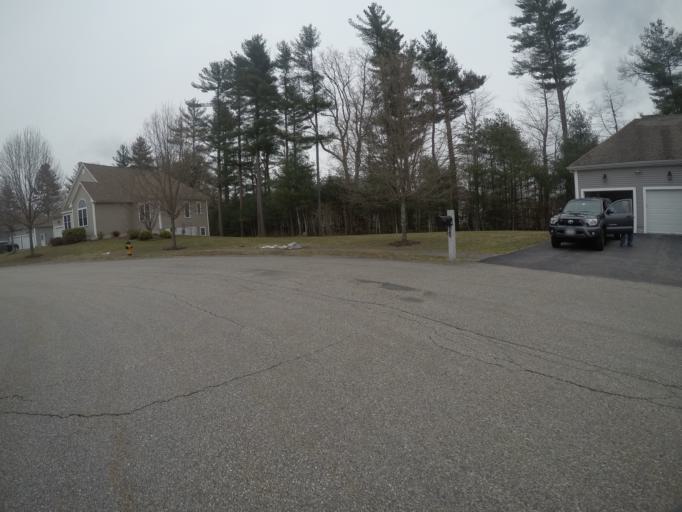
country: US
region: Massachusetts
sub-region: Bristol County
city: Easton
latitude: 42.0300
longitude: -71.1534
